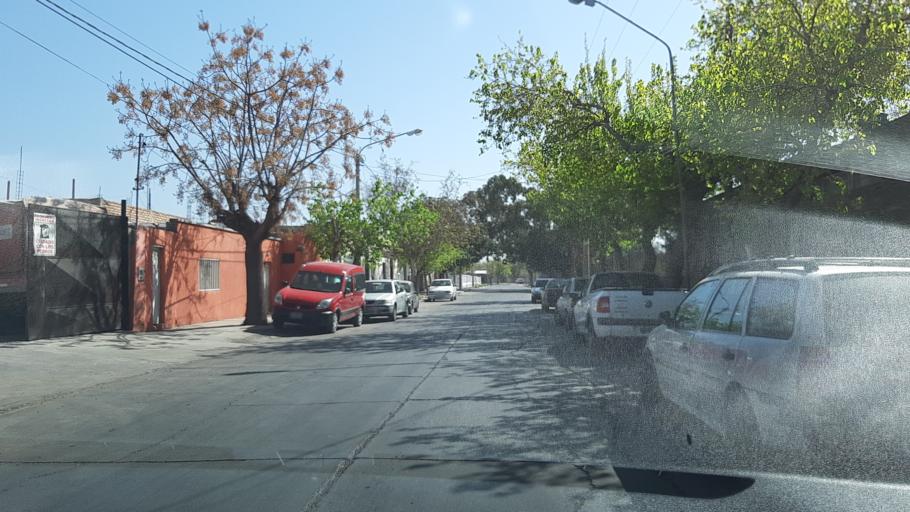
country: AR
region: San Juan
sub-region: Departamento de Santa Lucia
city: Santa Lucia
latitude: -31.5301
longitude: -68.5119
